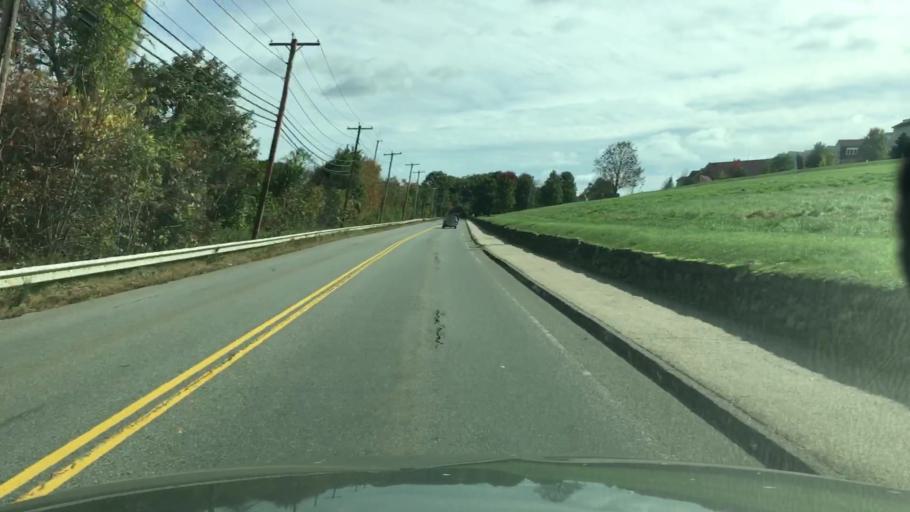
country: US
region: Massachusetts
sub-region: Worcester County
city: Charlton
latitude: 42.1419
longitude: -71.9796
